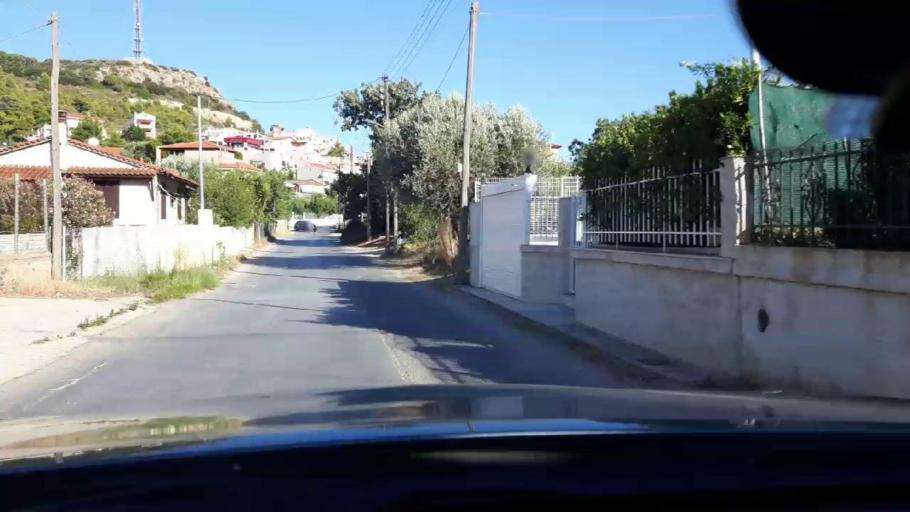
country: GR
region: Attica
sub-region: Nomarchia Anatolikis Attikis
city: Limin Mesoyaias
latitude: 37.8812
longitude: 24.0039
